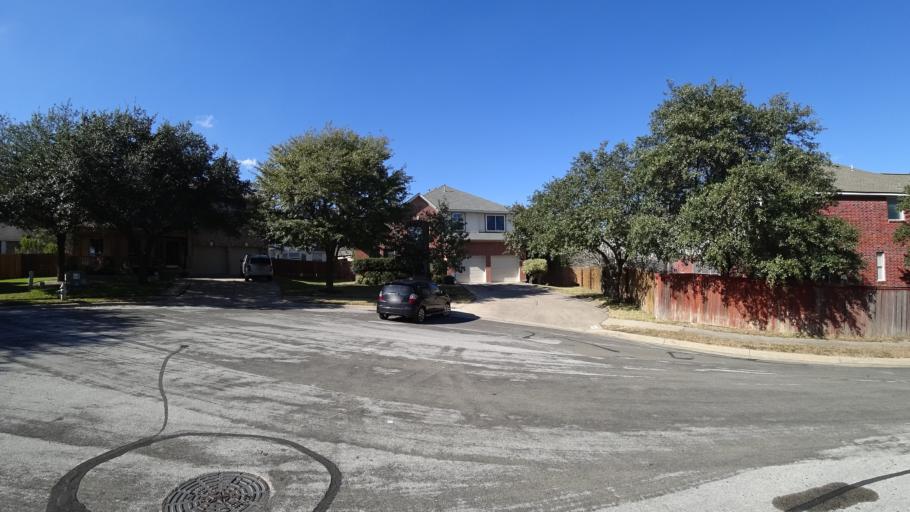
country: US
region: Texas
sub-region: Travis County
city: Wells Branch
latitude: 30.4265
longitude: -97.6868
